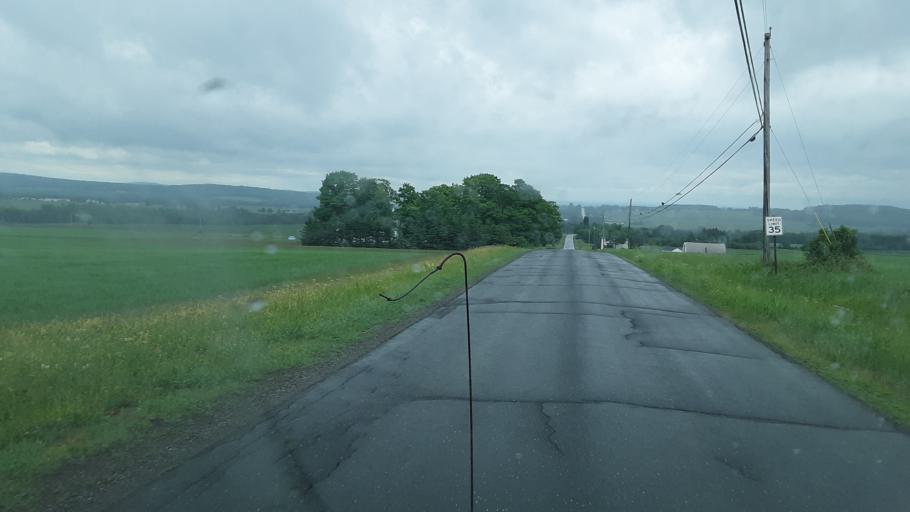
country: US
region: Maine
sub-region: Aroostook County
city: Presque Isle
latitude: 46.6818
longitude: -68.1837
